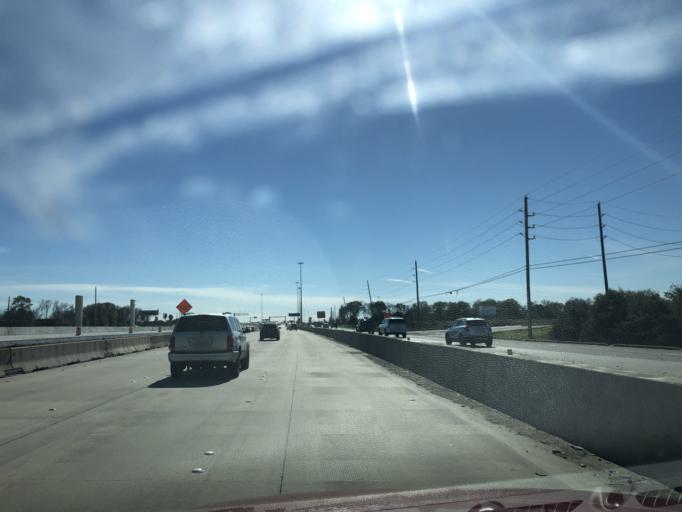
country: US
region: Texas
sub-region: Brazoria County
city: Brookside Village
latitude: 29.5895
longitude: -95.3868
